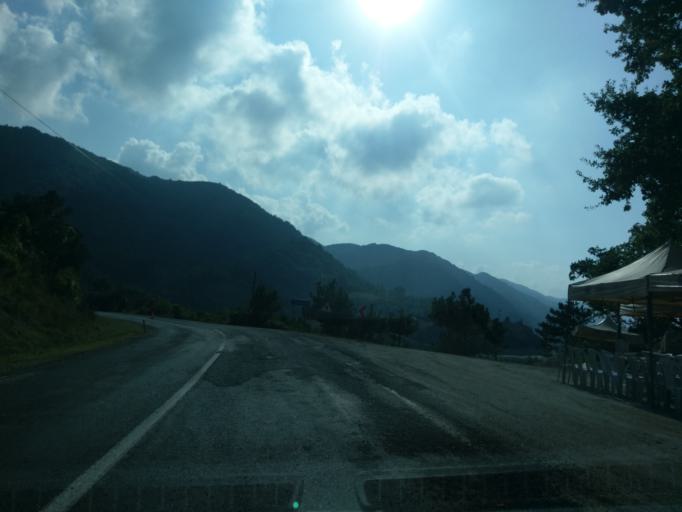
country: TR
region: Sinop
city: Ayancik
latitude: 41.9410
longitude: 34.6732
